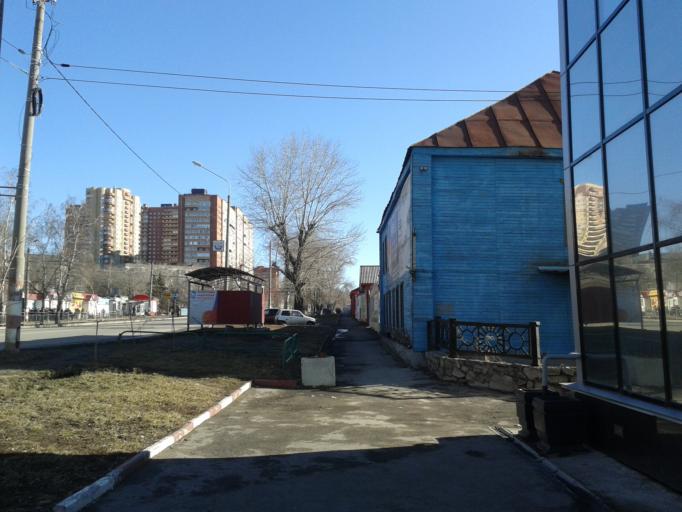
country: RU
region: Ulyanovsk
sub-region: Ulyanovskiy Rayon
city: Ulyanovsk
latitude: 54.2979
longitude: 48.3796
